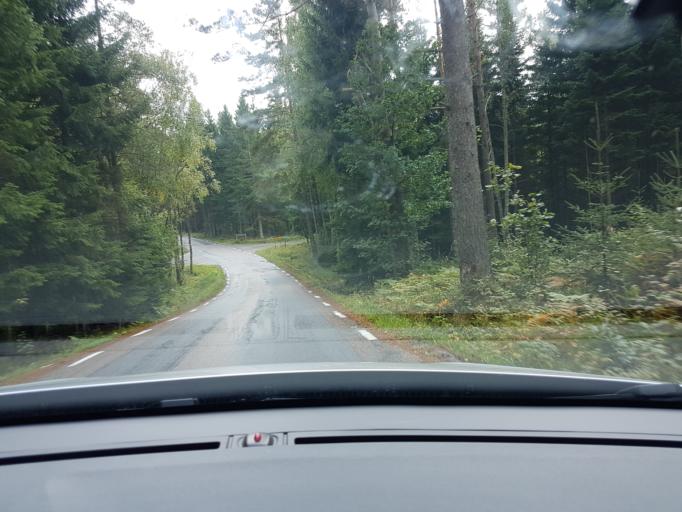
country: SE
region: Vaestra Goetaland
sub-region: Ale Kommun
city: Skepplanda
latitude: 57.9003
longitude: 12.1852
